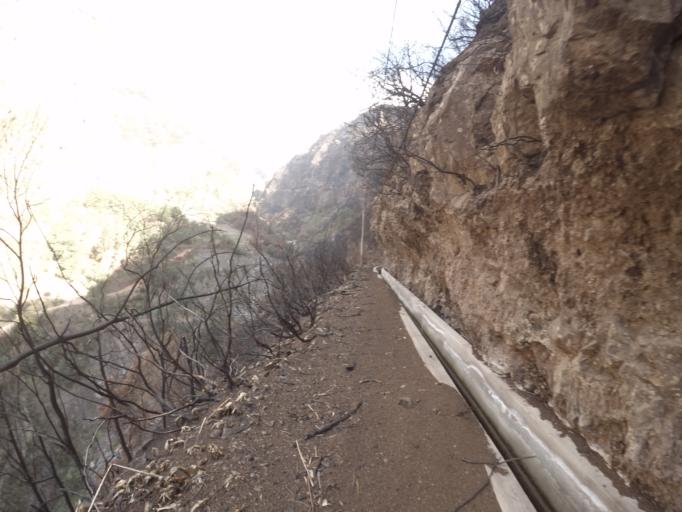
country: PT
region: Madeira
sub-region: Funchal
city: Nossa Senhora do Monte
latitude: 32.6894
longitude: -16.9160
